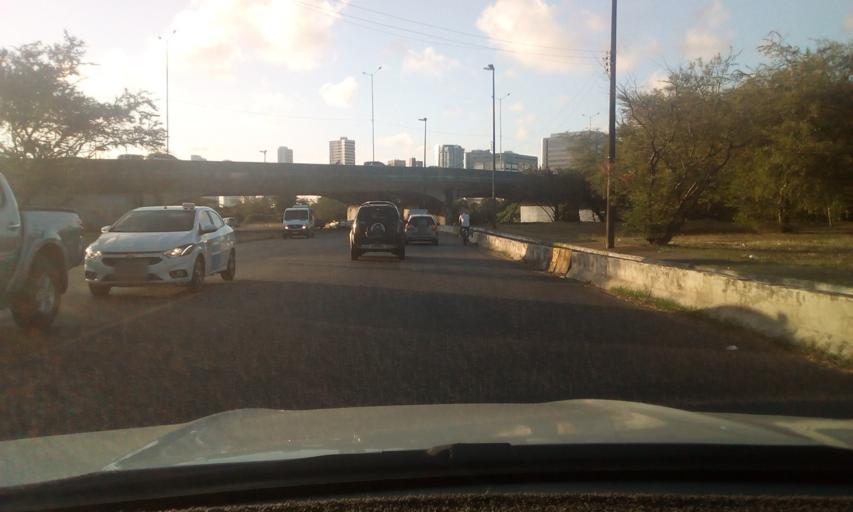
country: BR
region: Pernambuco
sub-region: Recife
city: Recife
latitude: -8.0691
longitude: -34.8958
